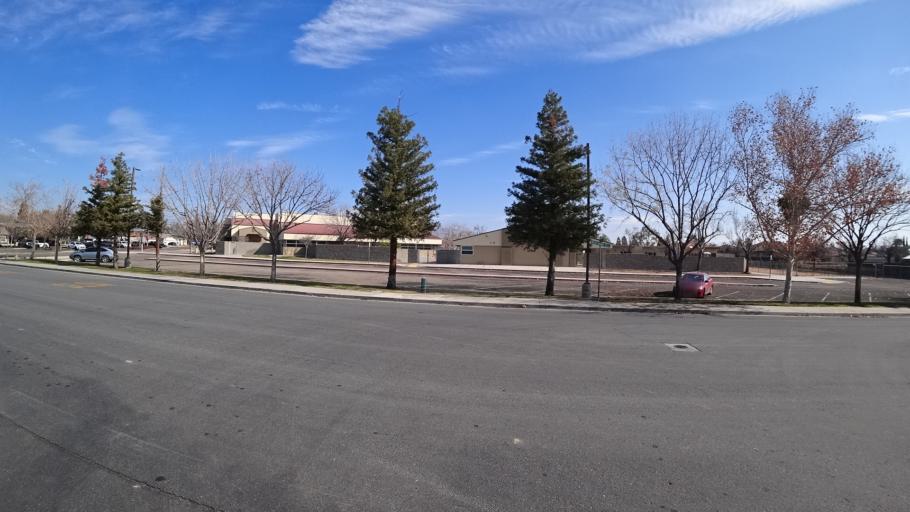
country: US
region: California
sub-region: Kern County
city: Lamont
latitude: 35.3916
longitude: -118.8820
